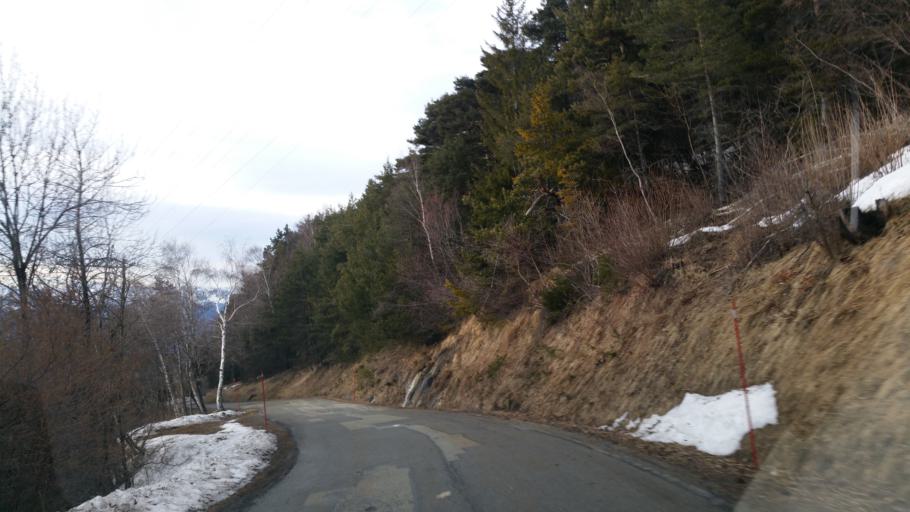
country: FR
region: Rhone-Alpes
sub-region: Departement de la Savoie
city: Villargondran
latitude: 45.2764
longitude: 6.3891
